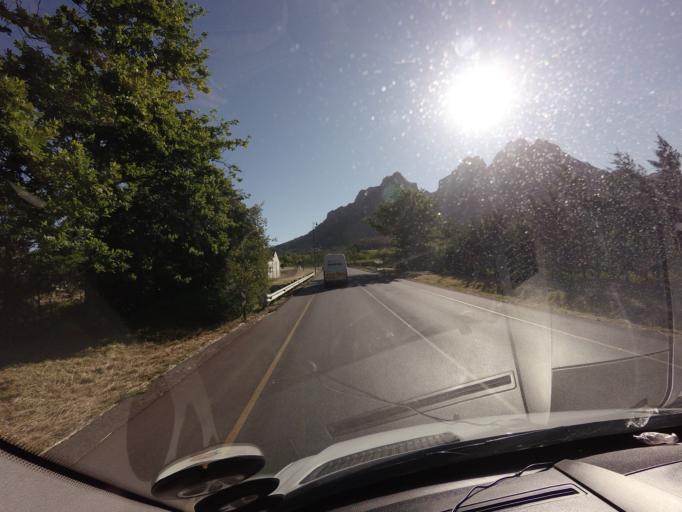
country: ZA
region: Western Cape
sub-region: Cape Winelands District Municipality
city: Stellenbosch
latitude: -33.8899
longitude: 18.9616
